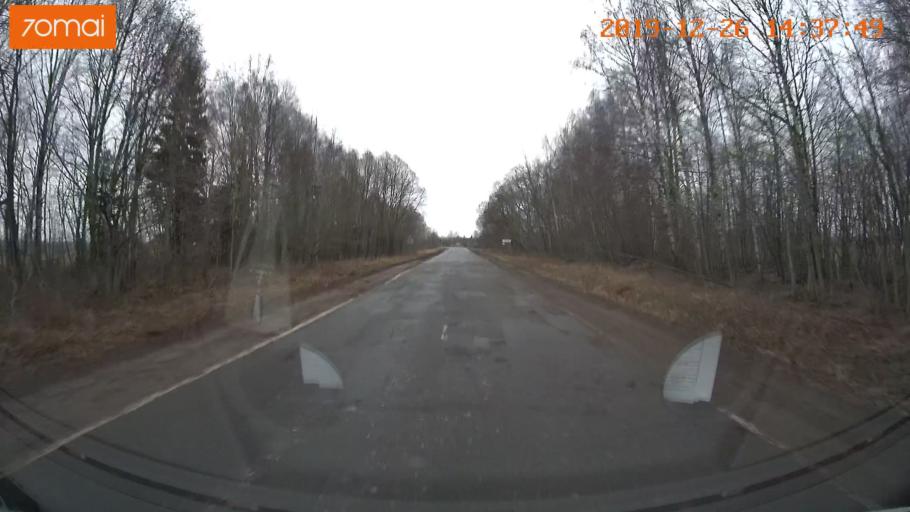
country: RU
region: Jaroslavl
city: Poshekhon'ye
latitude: 58.3993
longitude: 38.9717
